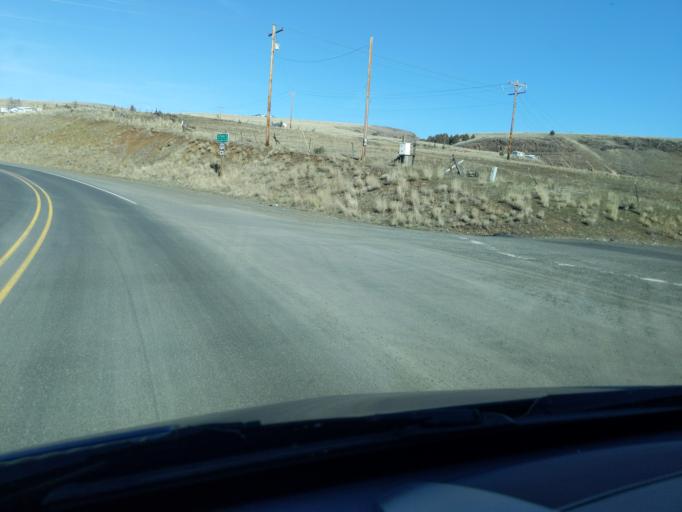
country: US
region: Oregon
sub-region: Grant County
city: John Day
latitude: 44.8363
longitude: -119.0310
